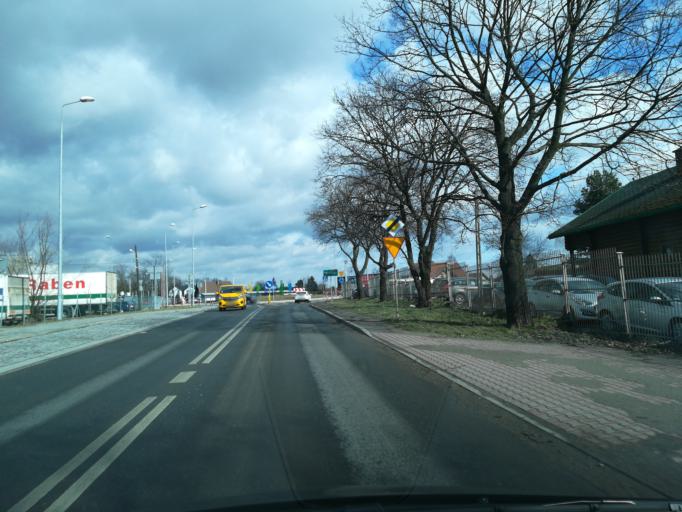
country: PL
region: Lesser Poland Voivodeship
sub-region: Powiat krakowski
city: Kryspinow
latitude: 50.0615
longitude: 19.8040
